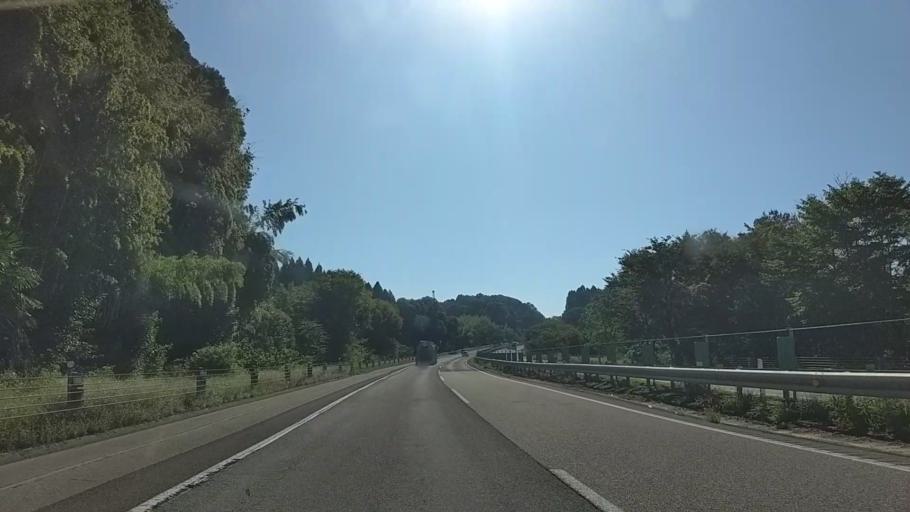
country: JP
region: Ishikawa
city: Tsubata
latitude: 36.6028
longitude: 136.7269
